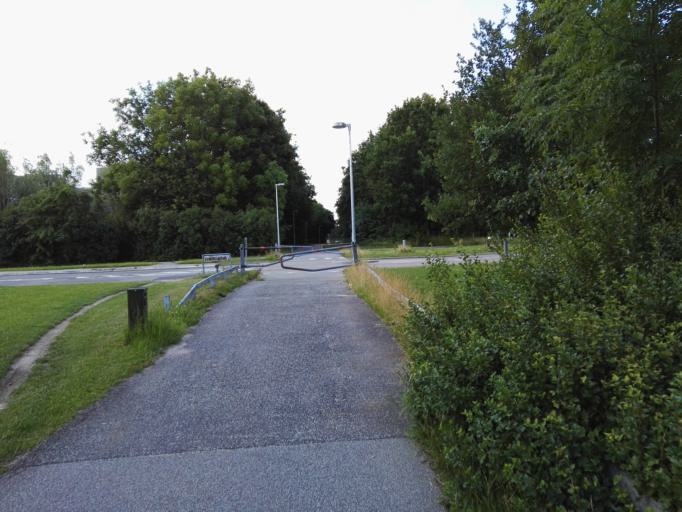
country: DK
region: Capital Region
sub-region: Ballerup Kommune
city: Ballerup
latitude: 55.7362
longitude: 12.3868
